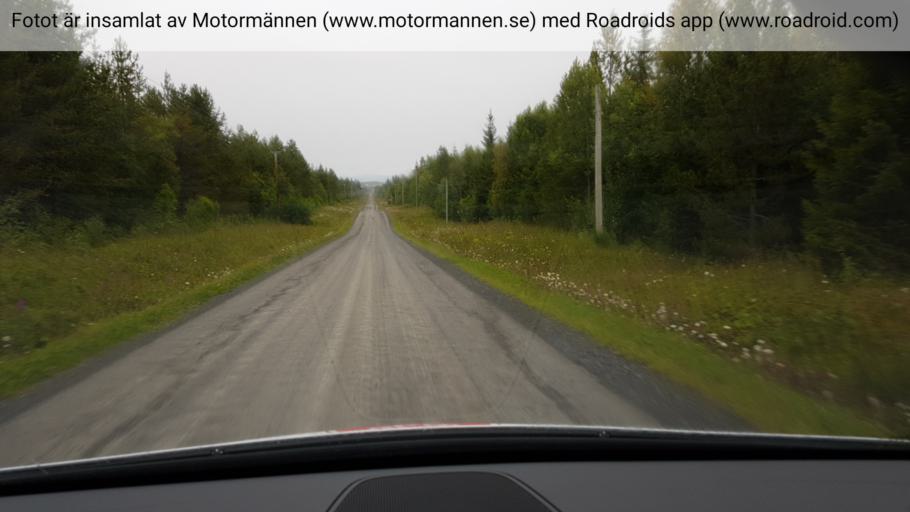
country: SE
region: Jaemtland
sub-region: OEstersunds Kommun
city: Lit
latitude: 63.6194
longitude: 14.9819
